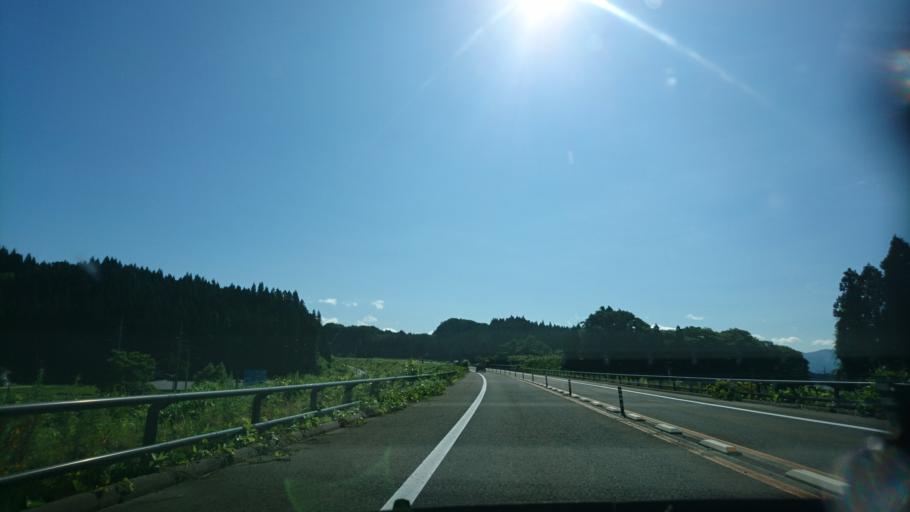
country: JP
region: Akita
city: Kakunodatemachi
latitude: 39.5946
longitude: 140.5406
